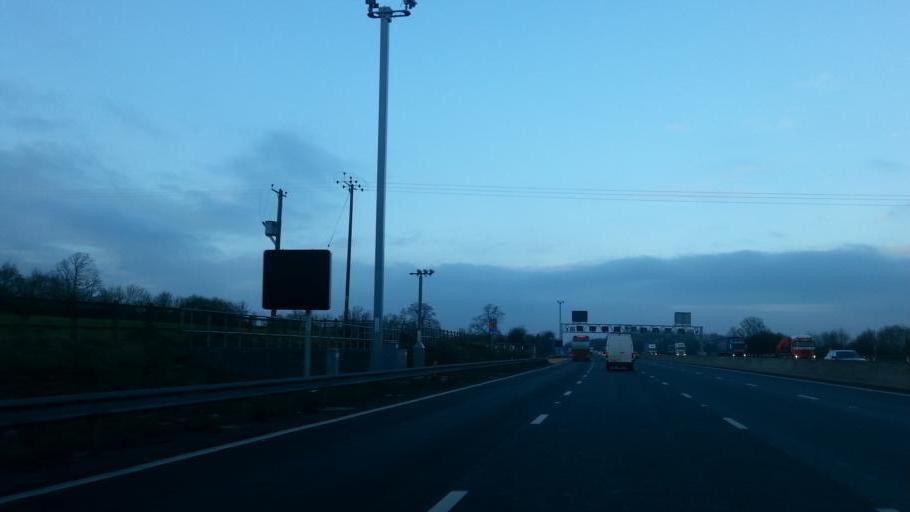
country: GB
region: England
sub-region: Worcestershire
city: Droitwich
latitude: 52.2477
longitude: -2.1335
